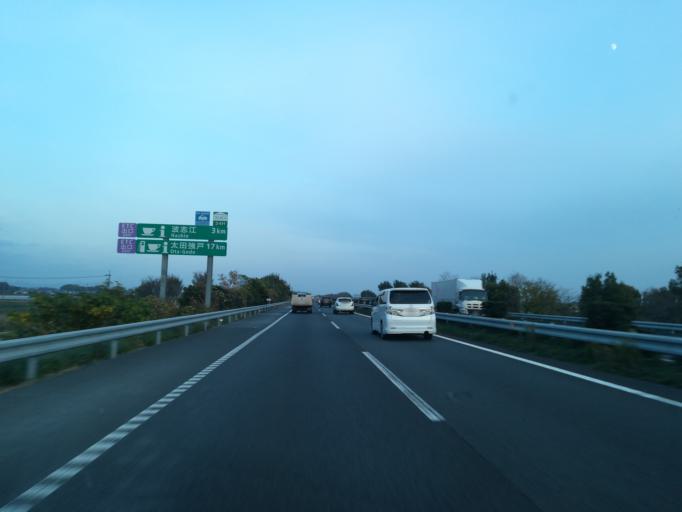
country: JP
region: Gunma
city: Isesaki
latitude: 36.3512
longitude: 139.1560
